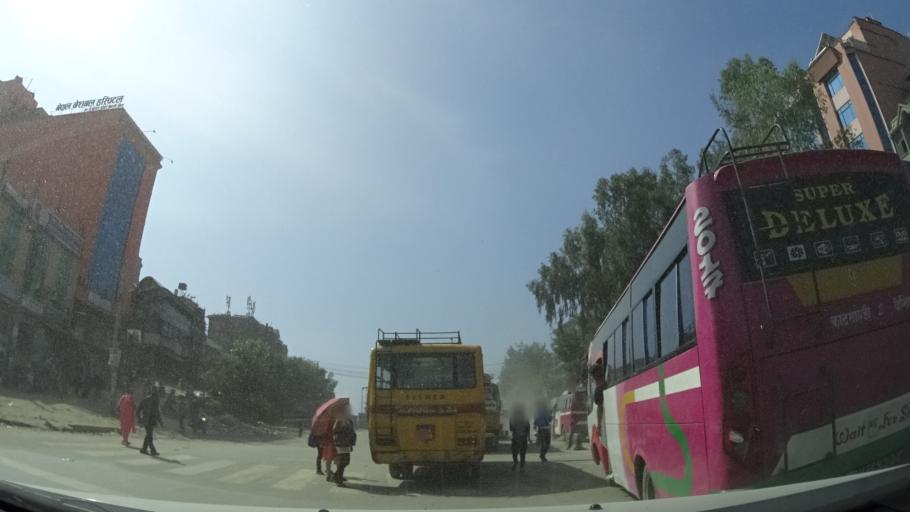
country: NP
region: Central Region
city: Kirtipur
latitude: 27.6952
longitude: 85.2817
